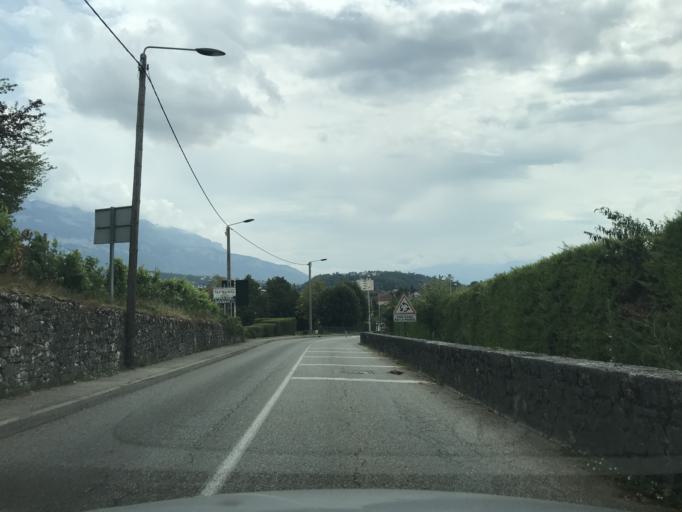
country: FR
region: Rhone-Alpes
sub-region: Departement de la Savoie
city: Brison-Saint-Innocent
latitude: 45.7106
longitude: 5.8934
